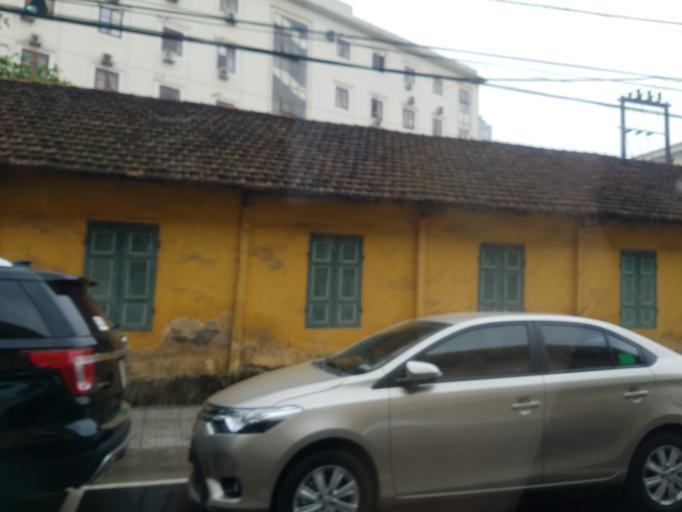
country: VN
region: Thai Nguyen
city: Thanh Pho Thai Nguyen
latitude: 21.5941
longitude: 105.8425
